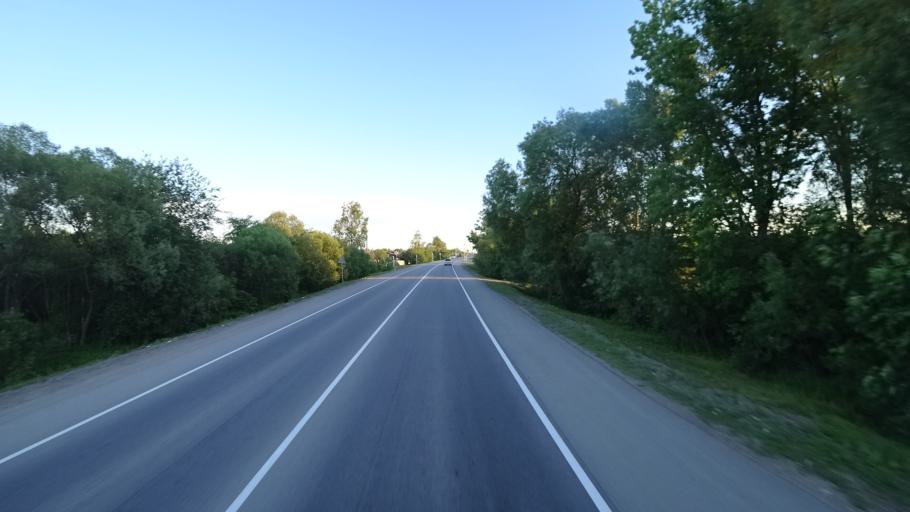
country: RU
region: Khabarovsk Krai
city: Khor
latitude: 47.8556
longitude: 134.9619
